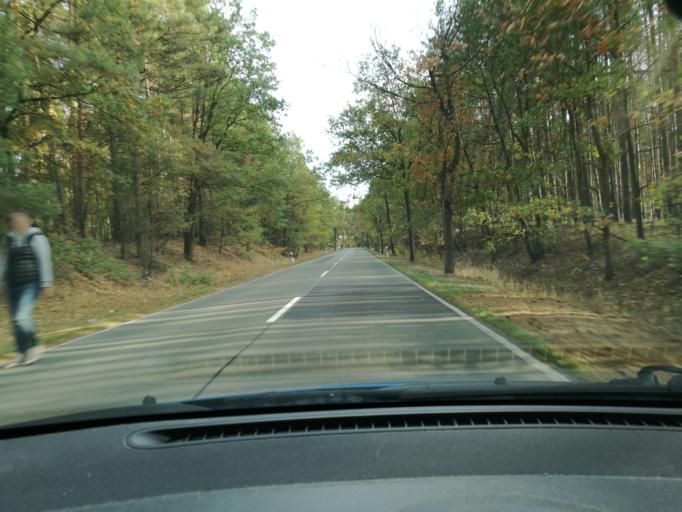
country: DE
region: Saxony-Anhalt
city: Luftkurort Arendsee
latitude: 52.8812
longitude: 11.4529
